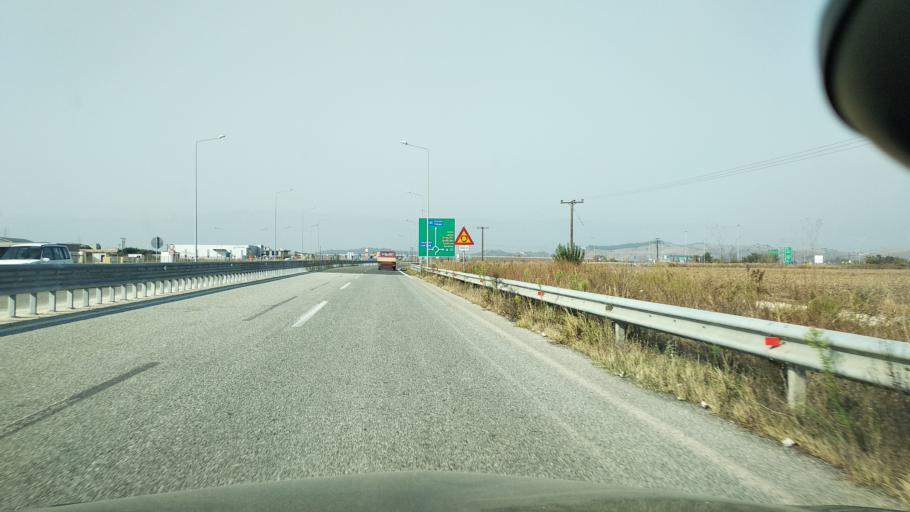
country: GR
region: Thessaly
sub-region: Trikala
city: Megalochori
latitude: 39.5668
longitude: 21.8249
